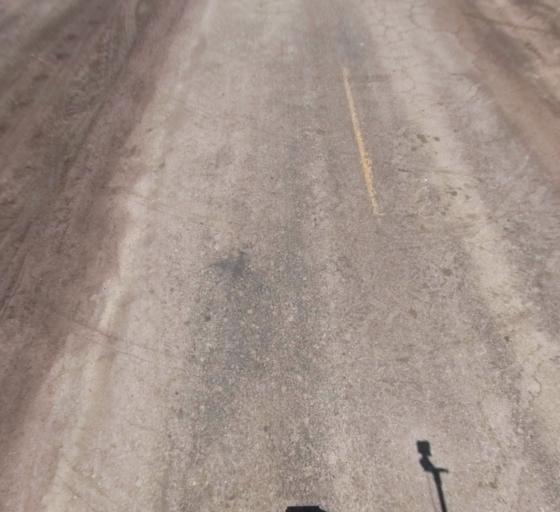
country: US
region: California
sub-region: Fresno County
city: Biola
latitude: 36.8583
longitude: -119.9831
